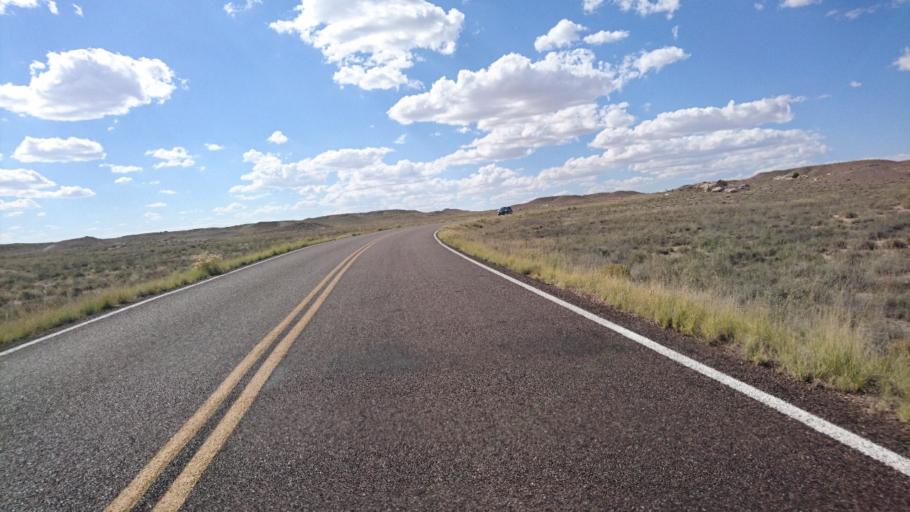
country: US
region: Arizona
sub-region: Navajo County
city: Holbrook
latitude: 34.8875
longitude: -109.8024
